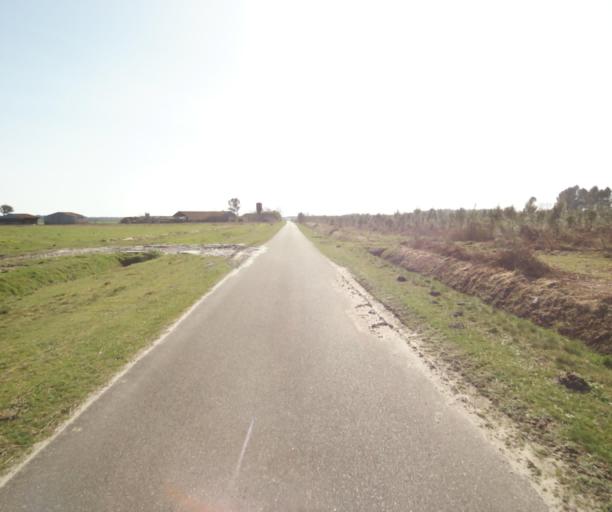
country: FR
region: Aquitaine
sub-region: Departement des Landes
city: Roquefort
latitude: 44.1624
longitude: -0.2509
